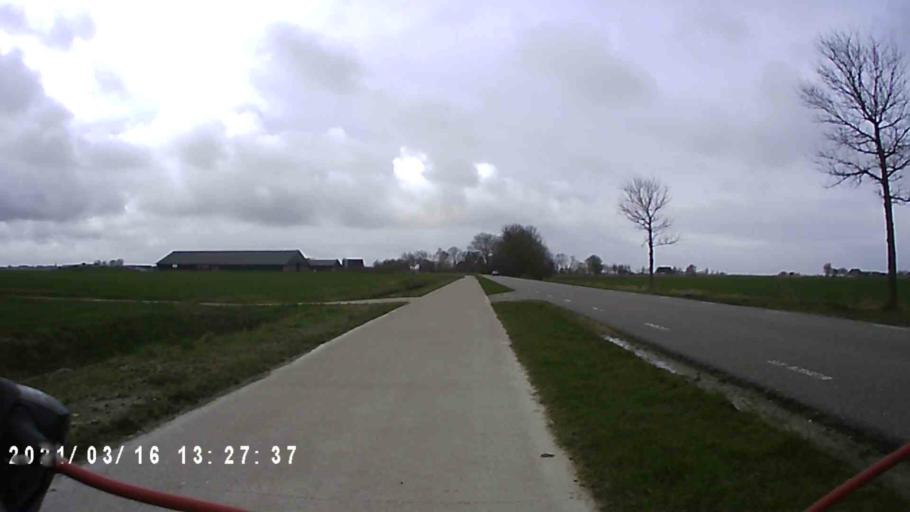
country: NL
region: Friesland
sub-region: Gemeente Franekeradeel
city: Tzummarum
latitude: 53.2178
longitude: 5.5726
